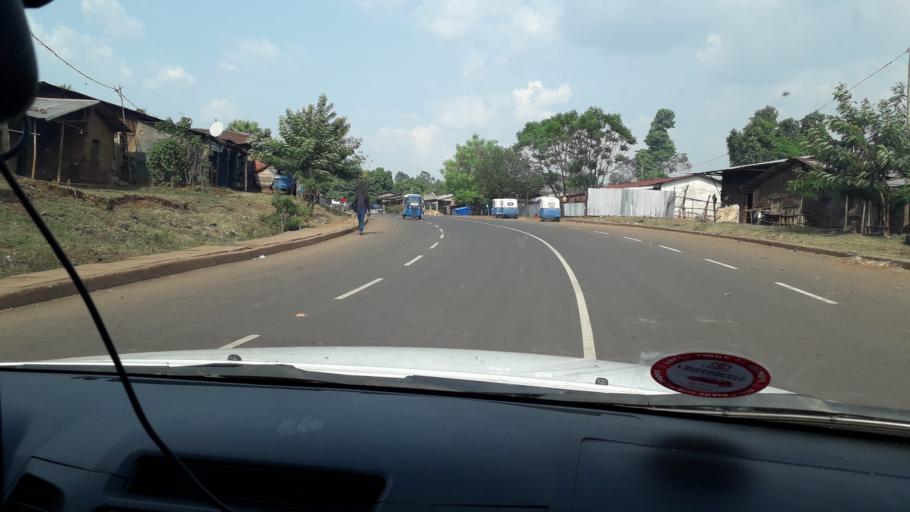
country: ET
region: Southern Nations, Nationalities, and People's Region
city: Mizan Teferi
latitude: 6.8554
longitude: 35.3326
